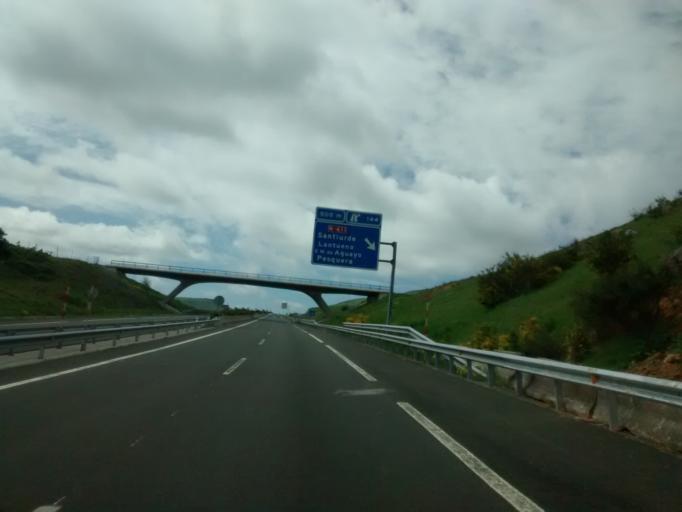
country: ES
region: Cantabria
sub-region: Provincia de Cantabria
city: Pesquera
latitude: 43.0784
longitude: -4.0861
